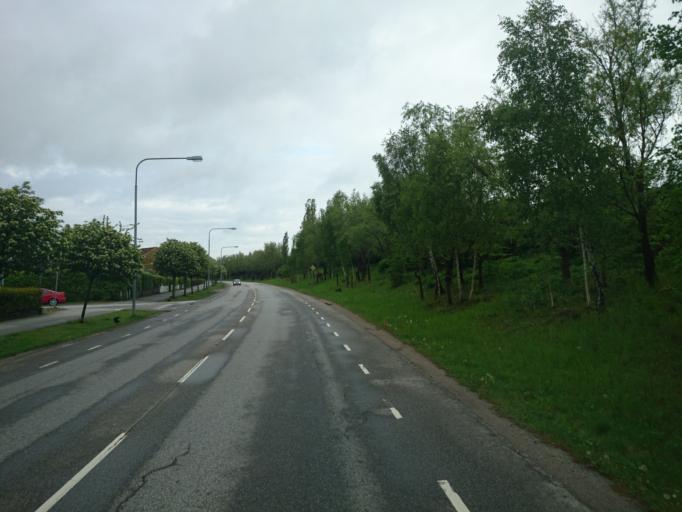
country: SE
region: Skane
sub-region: Burlovs Kommun
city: Arloev
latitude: 55.6131
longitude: 13.0633
